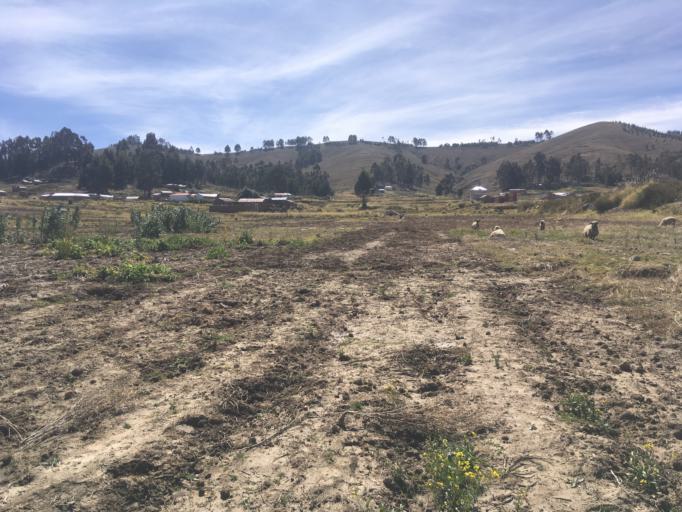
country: BO
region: La Paz
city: San Pedro
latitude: -16.2632
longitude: -68.8740
